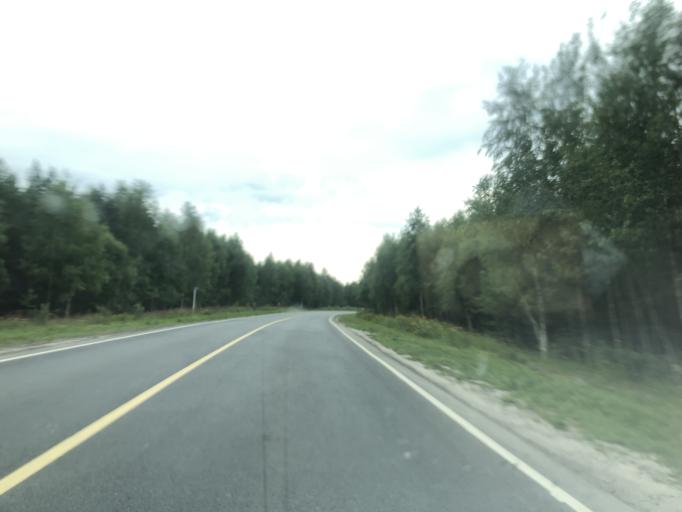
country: RU
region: Ivanovo
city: Pestyaki
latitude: 56.7084
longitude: 42.7817
